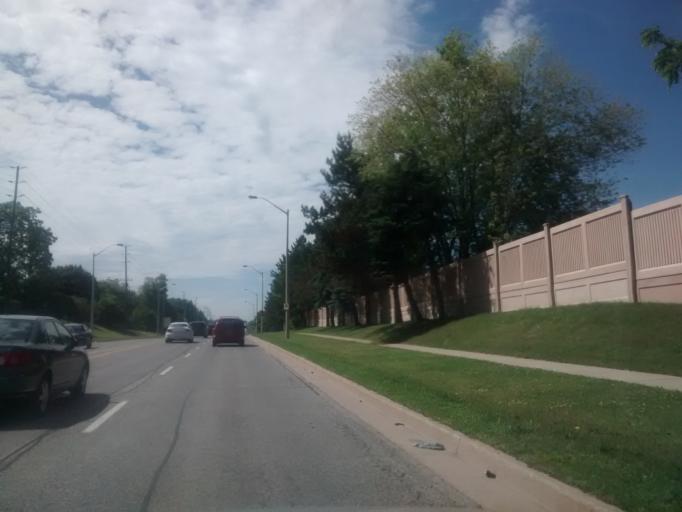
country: CA
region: Ontario
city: Burlington
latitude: 43.3683
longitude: -79.8268
